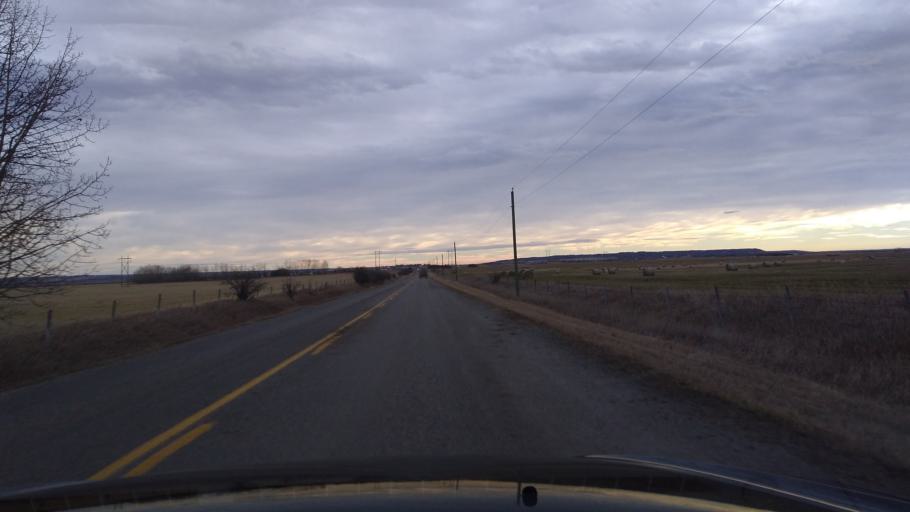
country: CA
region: Alberta
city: Cochrane
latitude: 51.0960
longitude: -114.4194
